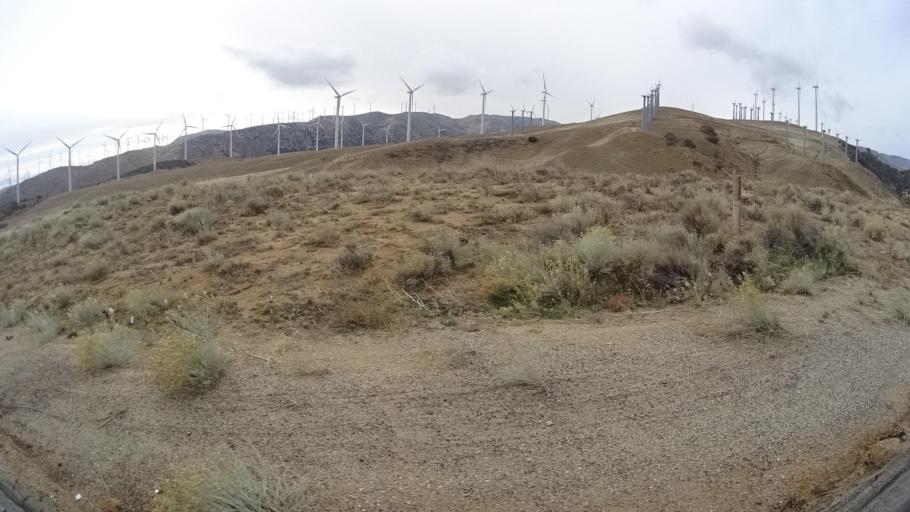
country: US
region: California
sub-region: Kern County
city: Tehachapi
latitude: 35.0567
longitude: -118.3796
